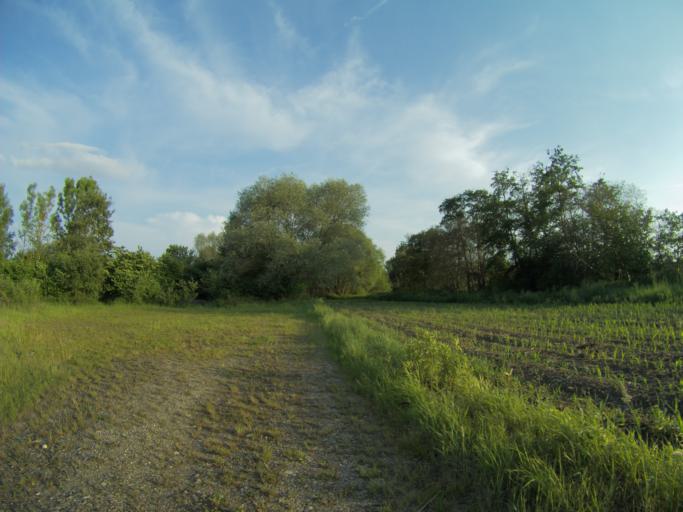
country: DE
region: Bavaria
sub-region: Upper Bavaria
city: Freising
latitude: 48.3704
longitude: 11.7646
